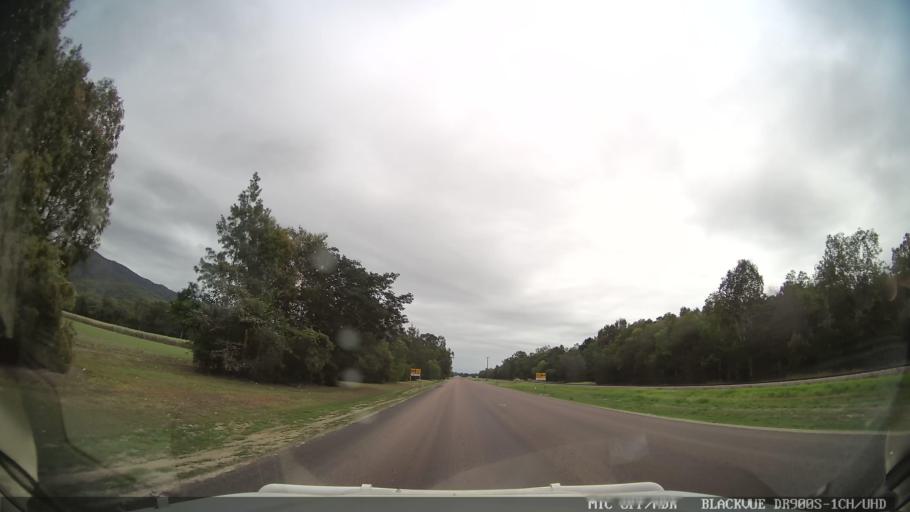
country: AU
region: Queensland
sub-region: Hinchinbrook
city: Ingham
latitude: -18.9308
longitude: 146.2668
